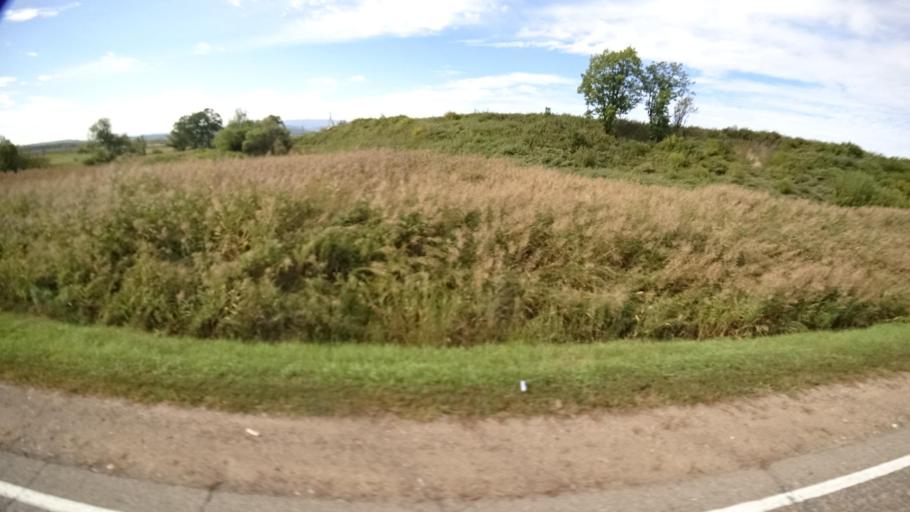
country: RU
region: Primorskiy
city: Dostoyevka
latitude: 44.3134
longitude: 133.4610
